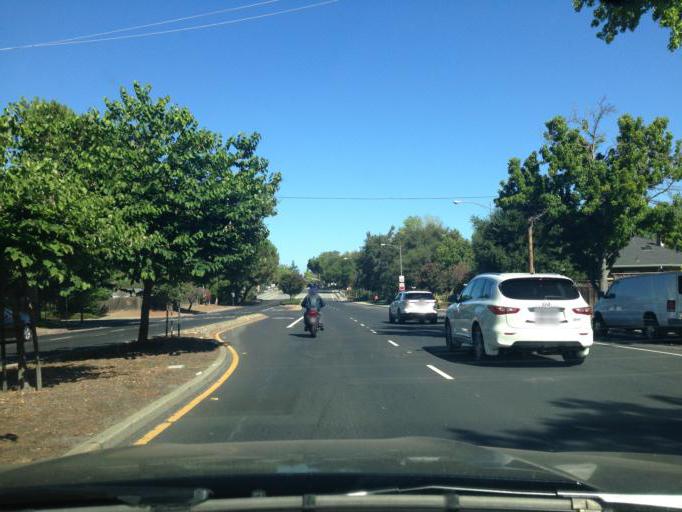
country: US
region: California
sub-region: Santa Clara County
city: Los Gatos
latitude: 37.2512
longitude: -121.9626
